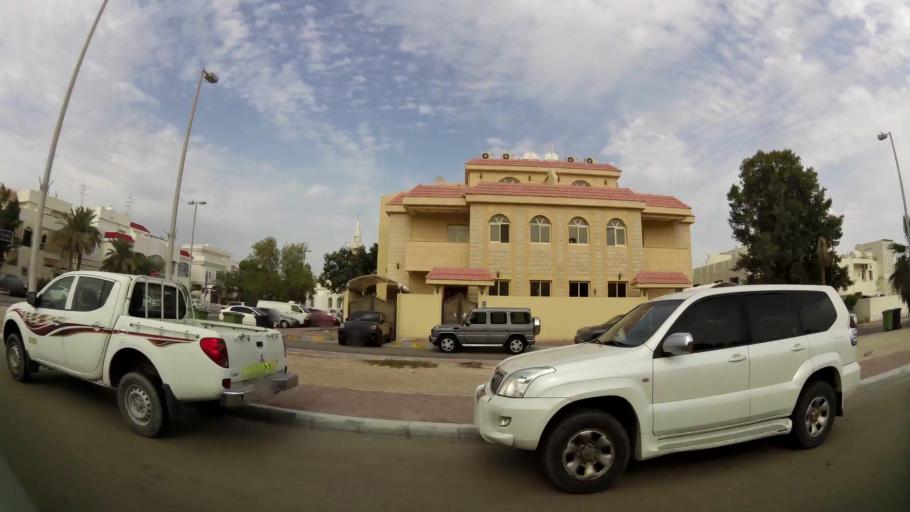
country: AE
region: Abu Dhabi
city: Abu Dhabi
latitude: 24.4629
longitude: 54.3529
